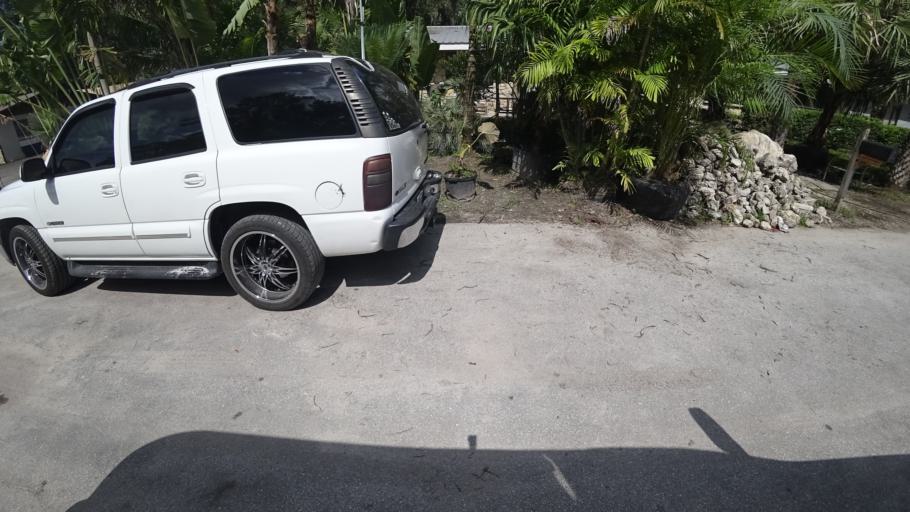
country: US
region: Florida
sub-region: Manatee County
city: Samoset
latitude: 27.4530
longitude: -82.5435
